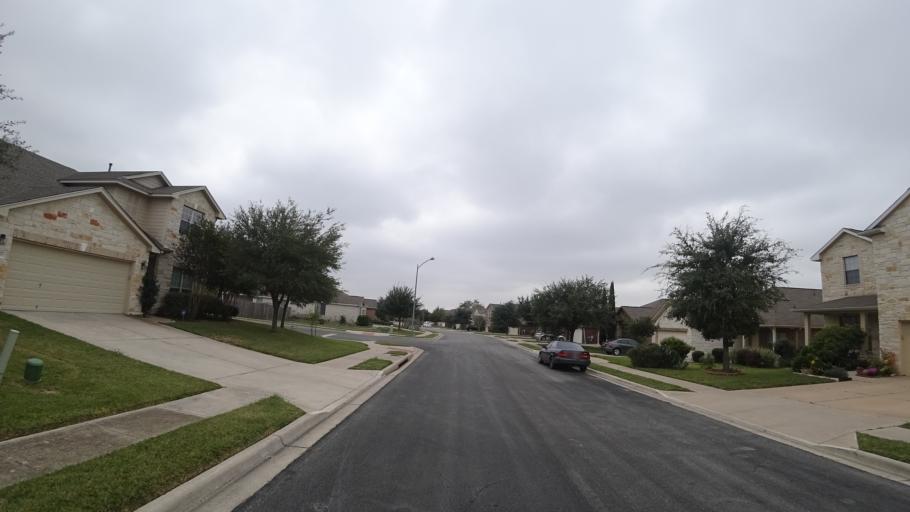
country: US
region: Texas
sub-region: Travis County
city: Pflugerville
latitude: 30.3749
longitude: -97.6492
